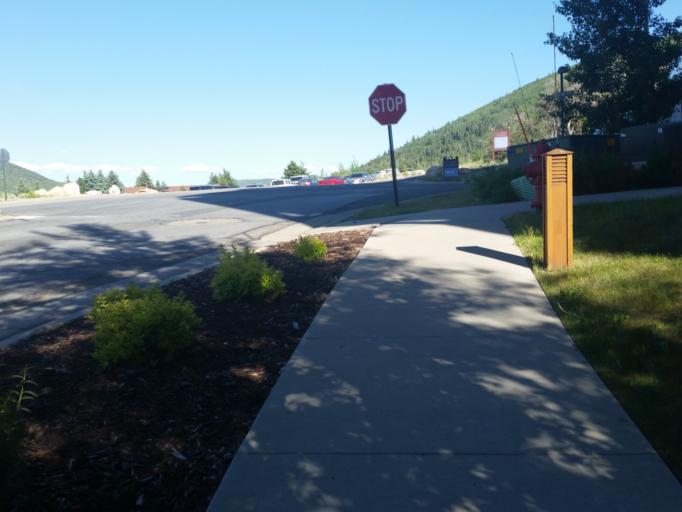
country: US
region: Utah
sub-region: Summit County
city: Snyderville
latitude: 40.6841
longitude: -111.5539
